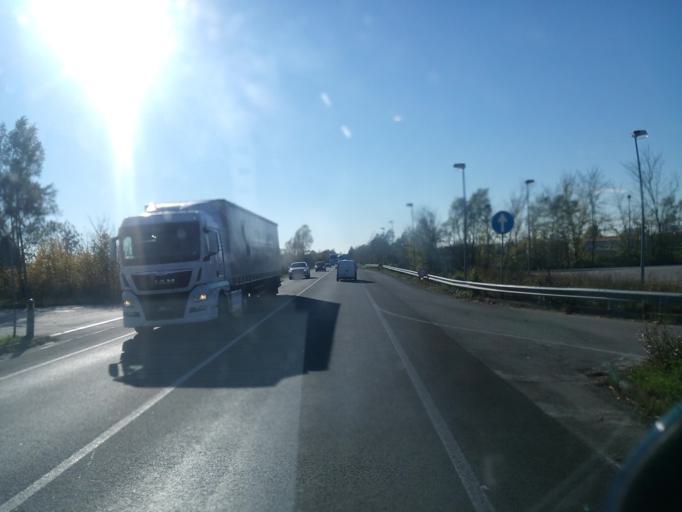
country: IT
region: Veneto
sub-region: Provincia di Padova
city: Borgoricco-San Michele delle Badesse-Sant'Eufemia
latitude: 45.5255
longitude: 11.9399
